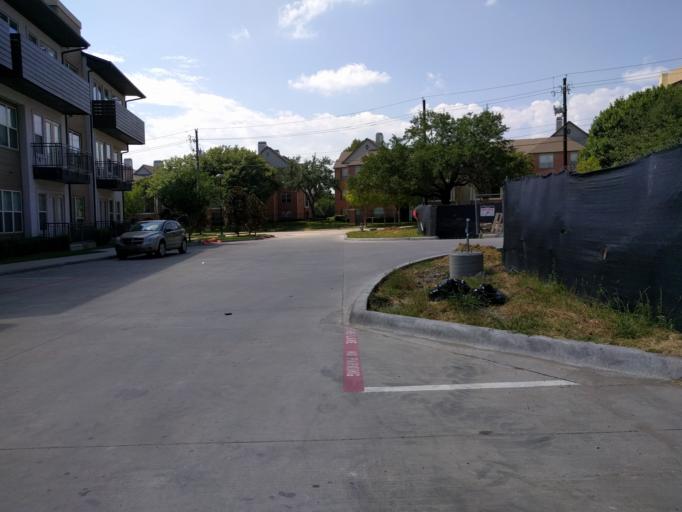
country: US
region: Texas
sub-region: Dallas County
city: Richardson
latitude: 32.9196
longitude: -96.7724
